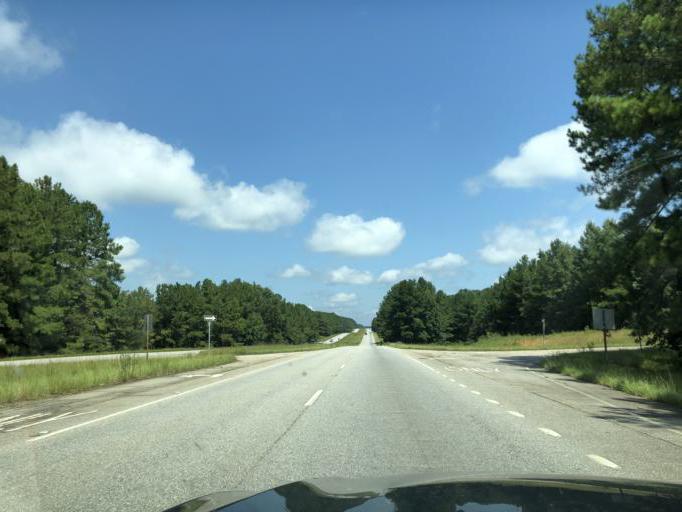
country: US
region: Alabama
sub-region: Henry County
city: Abbeville
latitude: 31.6557
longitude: -85.2801
